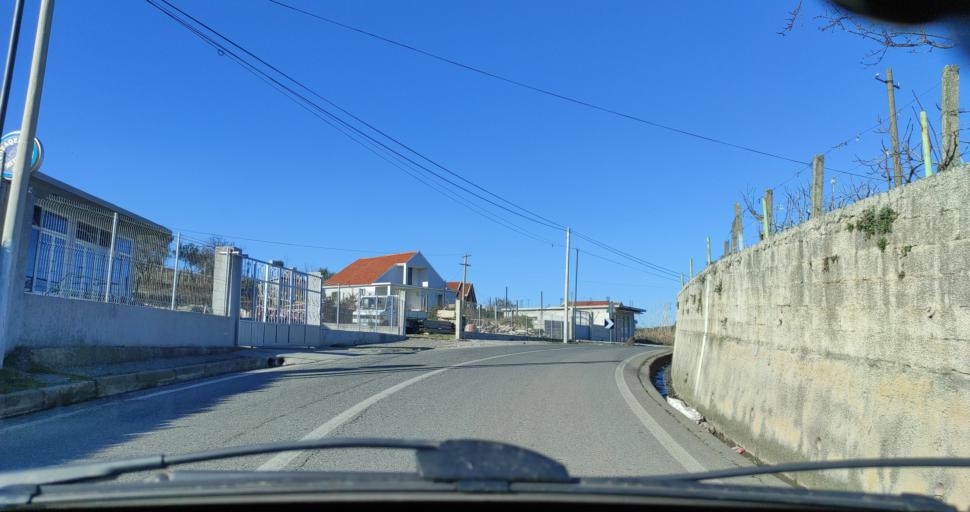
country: AL
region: Shkoder
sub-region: Rrethi i Shkodres
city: Velipoje
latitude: 41.9113
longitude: 19.4119
